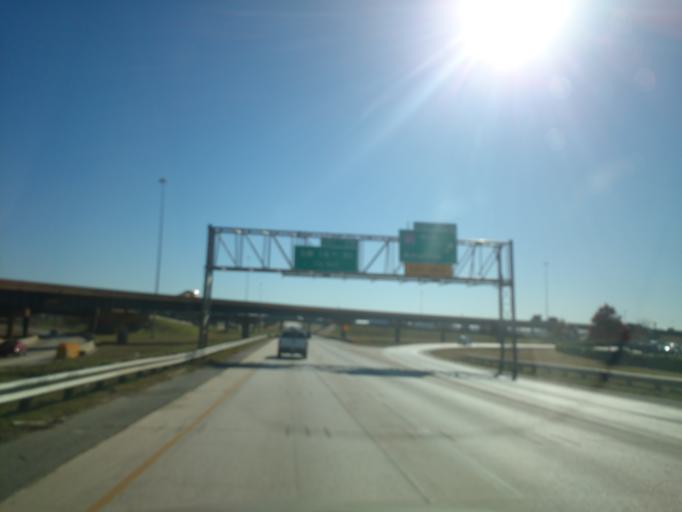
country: US
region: Oklahoma
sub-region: Oklahoma County
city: Oklahoma City
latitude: 35.4630
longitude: -97.5772
